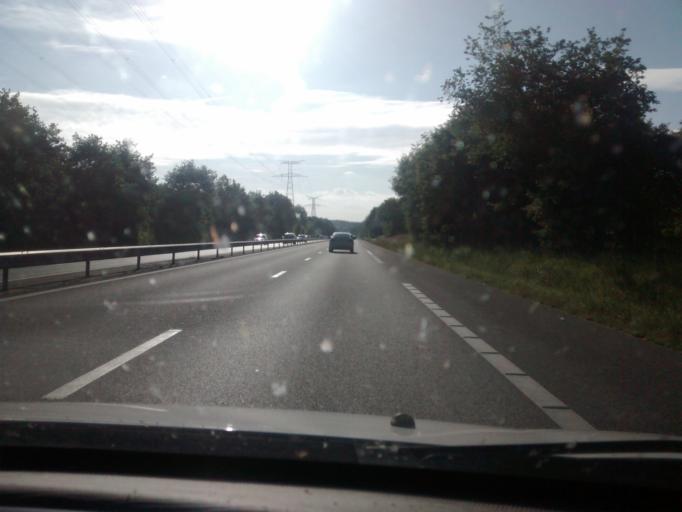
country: FR
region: Pays de la Loire
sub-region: Departement de la Mayenne
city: Saint-Pierre-la-Cour
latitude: 48.0854
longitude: -1.0550
